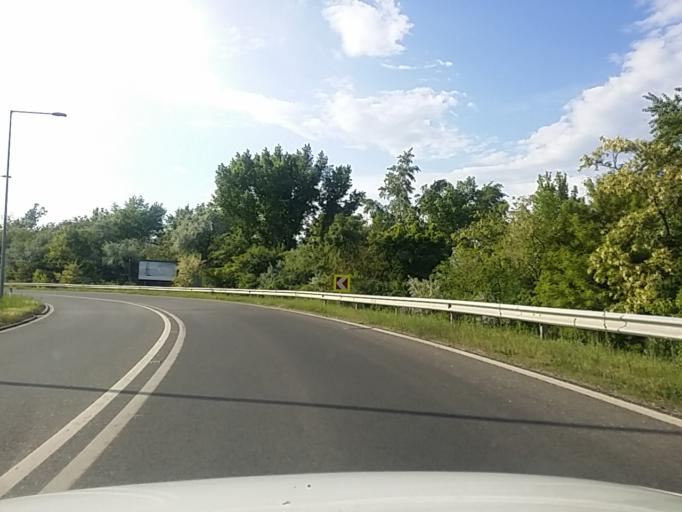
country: HU
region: Budapest
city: Budapest XV. keruelet
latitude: 47.6037
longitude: 19.1026
